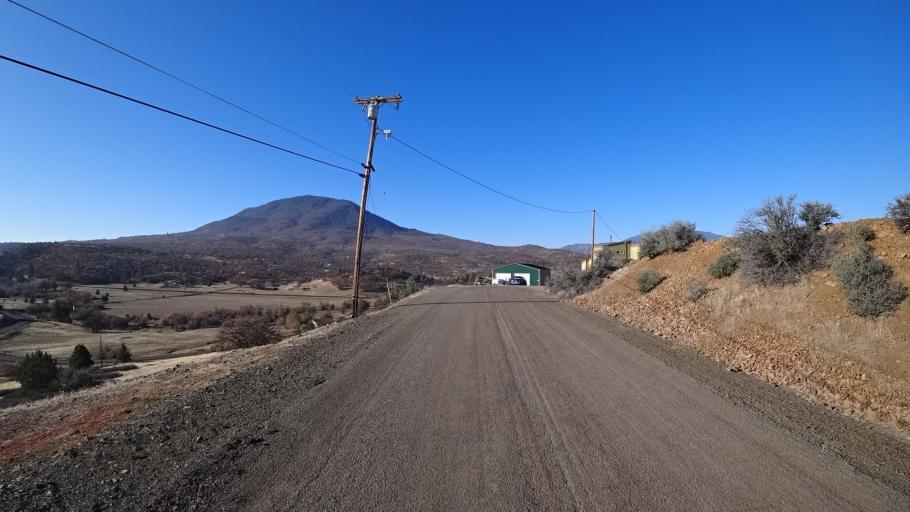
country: US
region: California
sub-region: Siskiyou County
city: Montague
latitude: 41.8947
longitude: -122.4814
